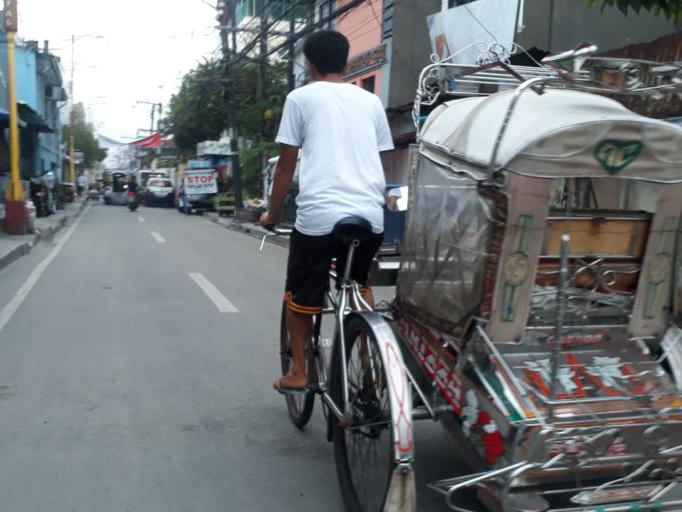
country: PH
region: Calabarzon
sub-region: Province of Rizal
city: Malabon
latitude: 14.6704
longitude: 120.9387
